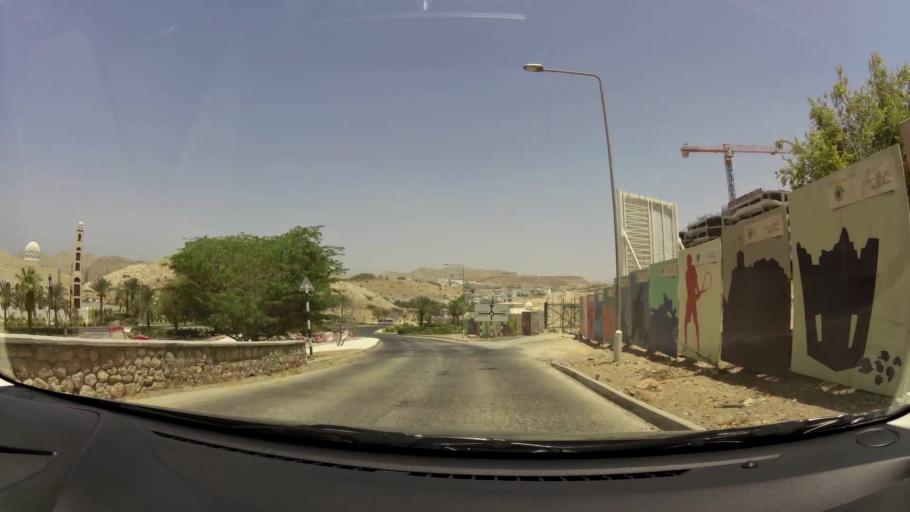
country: OM
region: Muhafazat Masqat
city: Muscat
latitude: 23.6256
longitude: 58.5033
